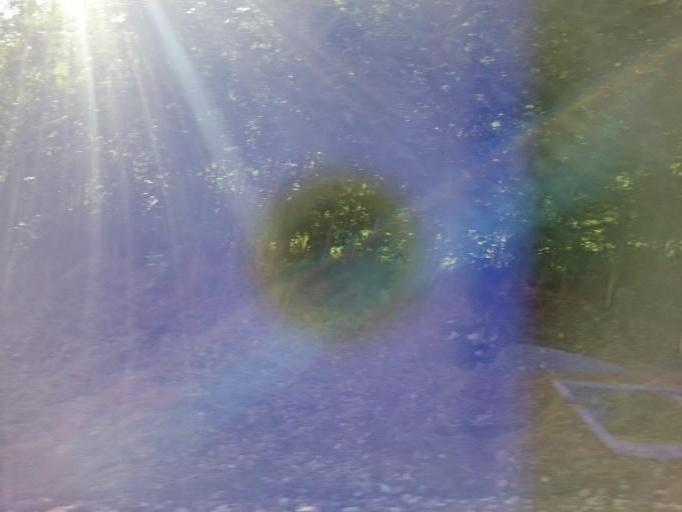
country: IT
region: Veneto
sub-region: Provincia di Verona
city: Dolce
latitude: 45.6032
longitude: 10.8519
